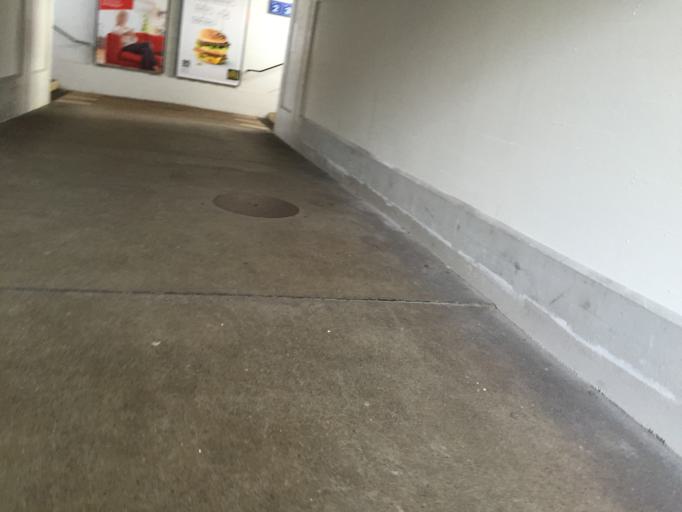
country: CH
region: Bern
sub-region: Bern-Mittelland District
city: Bolligen
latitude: 46.9566
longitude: 7.4816
